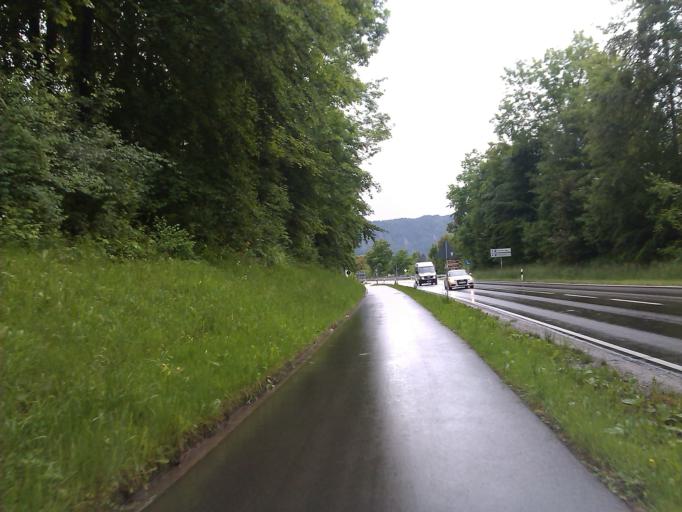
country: DE
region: Bavaria
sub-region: Swabia
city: Fuessen
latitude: 47.5893
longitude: 10.7075
